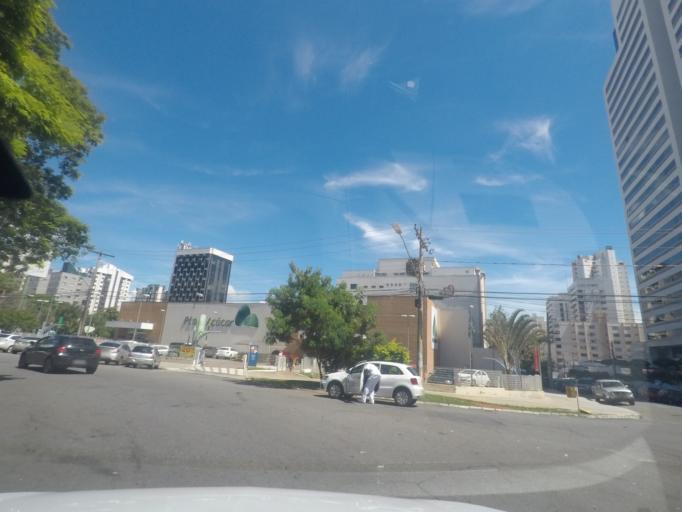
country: BR
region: Goias
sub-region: Goiania
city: Goiania
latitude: -16.6842
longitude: -49.2647
